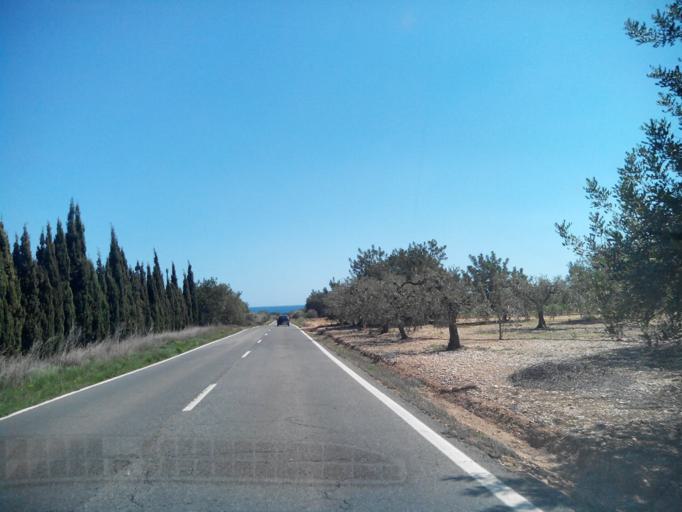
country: ES
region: Catalonia
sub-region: Provincia de Tarragona
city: Vilanova d'Escornalbou
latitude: 41.0738
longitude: 0.9738
